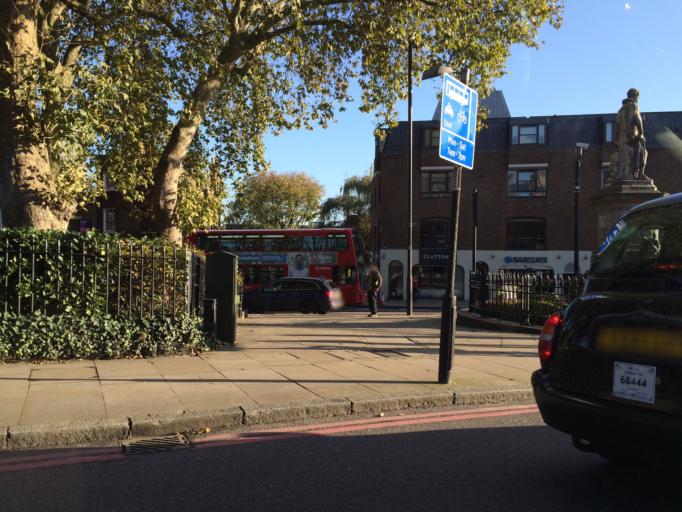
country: GB
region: England
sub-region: Greater London
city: Islington
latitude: 51.5358
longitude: -0.1037
